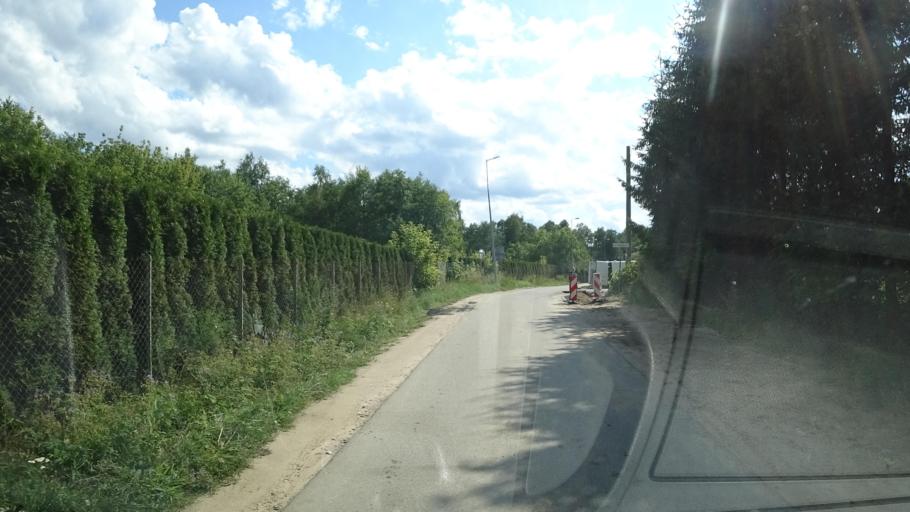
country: PL
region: Podlasie
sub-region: Powiat lomzynski
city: Piatnica
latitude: 53.1463
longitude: 22.1321
